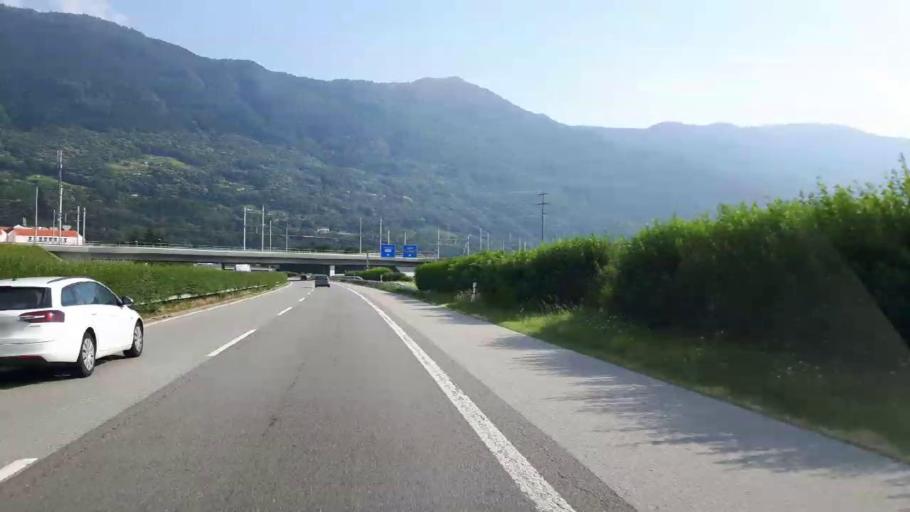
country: CH
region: Ticino
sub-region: Bellinzona District
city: Camorino
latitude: 46.1685
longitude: 8.9906
